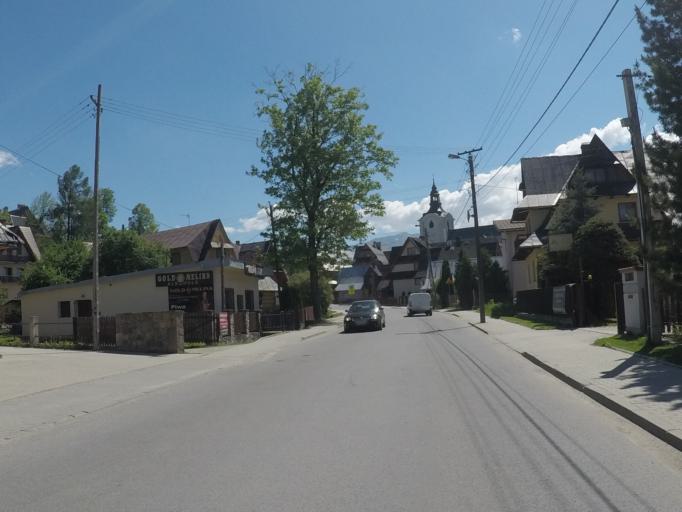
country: PL
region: Lesser Poland Voivodeship
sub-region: Powiat tatrzanski
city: Poronin
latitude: 49.3402
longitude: 20.0051
